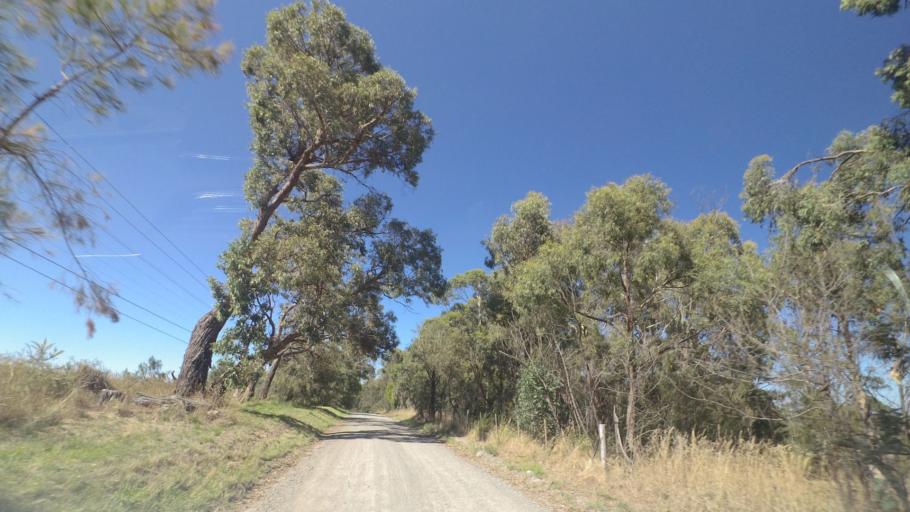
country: AU
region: Victoria
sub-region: Knox
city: Wantirna South
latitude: -37.8702
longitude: 145.2000
